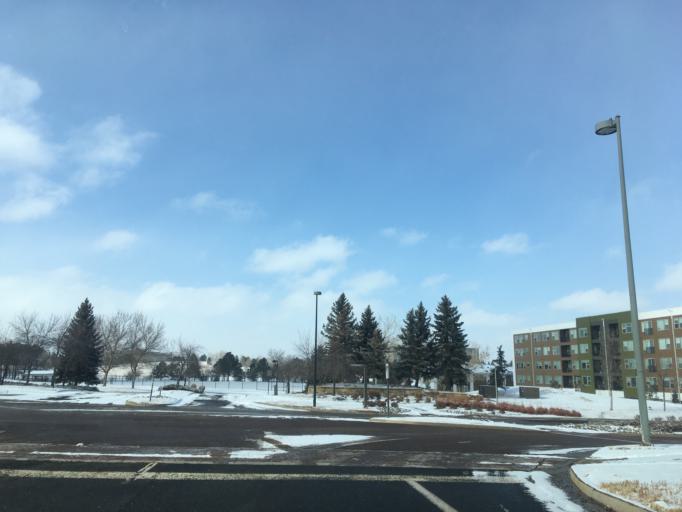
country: US
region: Colorado
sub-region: Broomfield County
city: Broomfield
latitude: 39.9218
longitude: -105.1233
